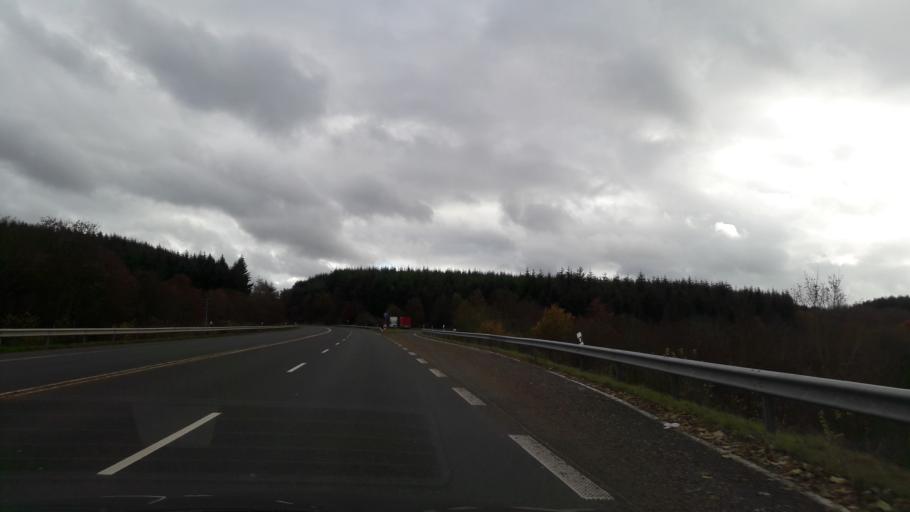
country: DE
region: Rheinland-Pfalz
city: Mertesdorf
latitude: 49.7707
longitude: 6.7539
